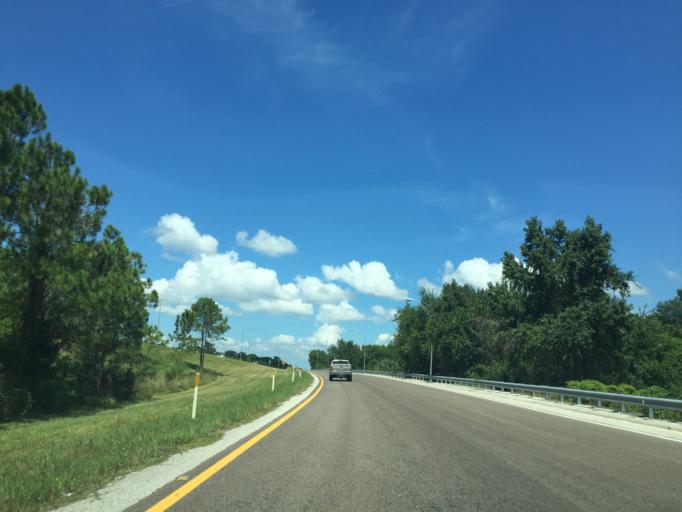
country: US
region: Florida
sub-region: Seminole County
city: Oviedo
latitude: 28.6914
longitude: -81.2274
